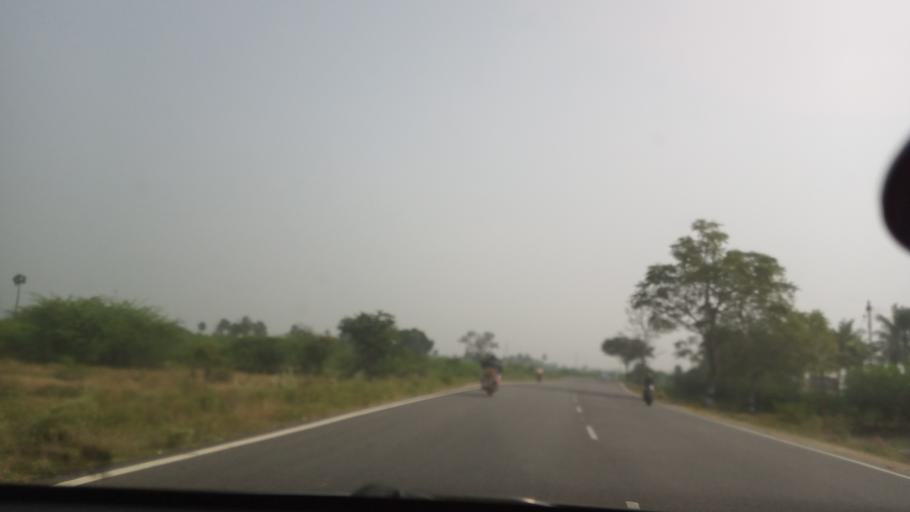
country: IN
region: Tamil Nadu
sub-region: Erode
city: Punjai Puliyampatti
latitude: 11.3866
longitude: 77.1769
